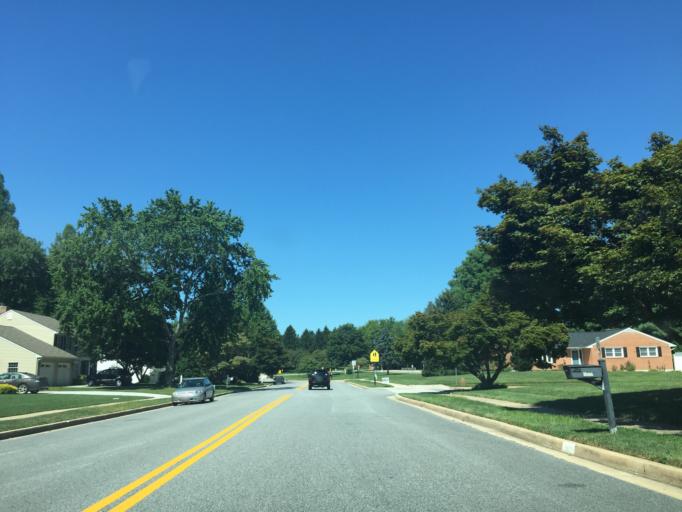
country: US
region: Maryland
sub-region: Baltimore County
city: Timonium
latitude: 39.4730
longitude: -76.6054
